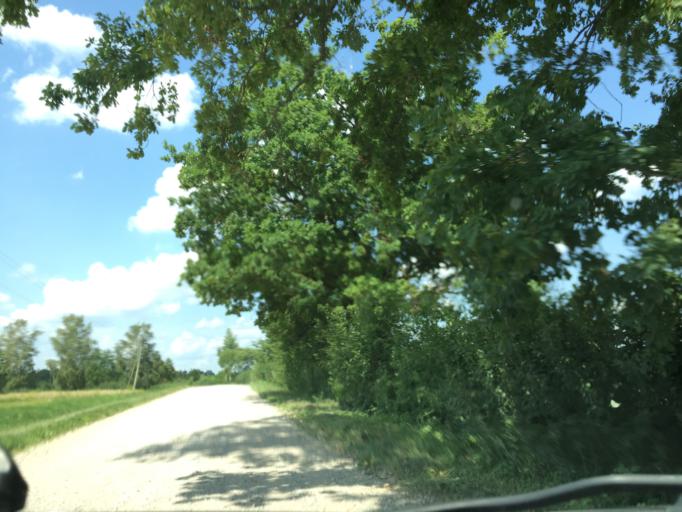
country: LT
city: Zagare
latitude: 56.3887
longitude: 23.2640
